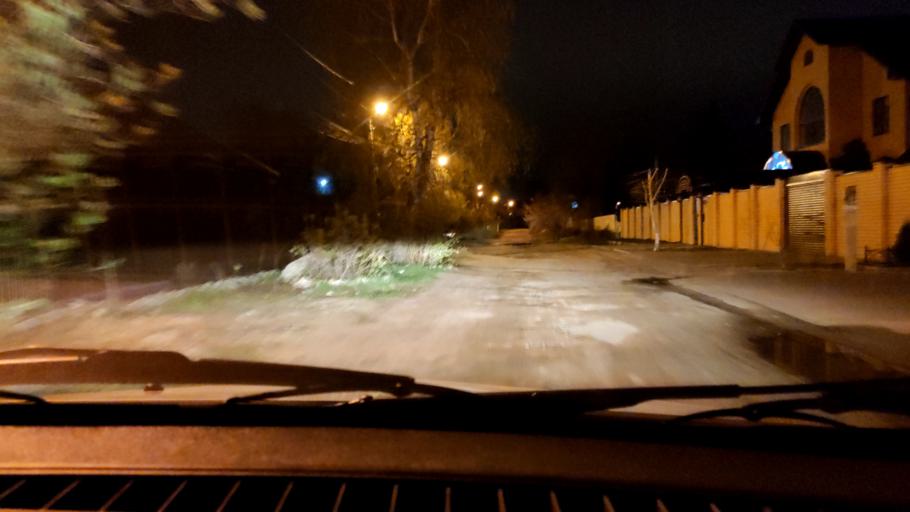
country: RU
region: Voronezj
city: Somovo
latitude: 51.7318
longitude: 39.2664
